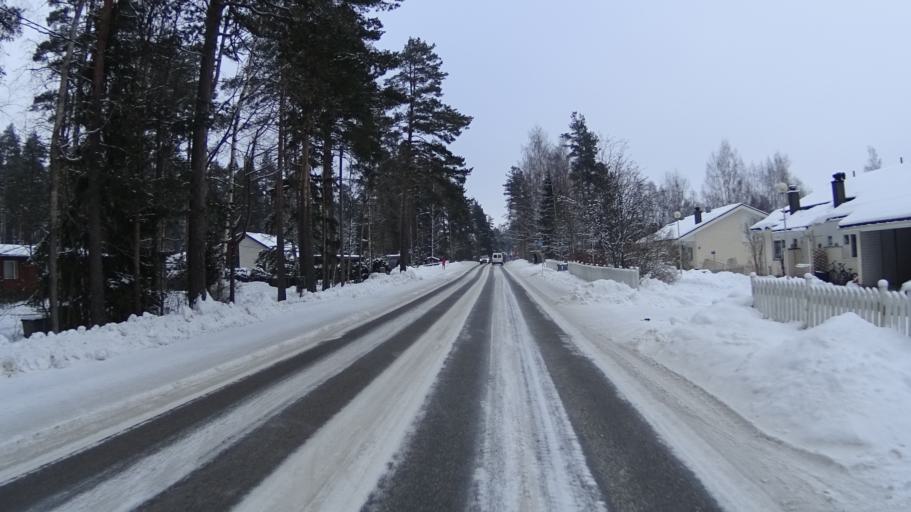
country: FI
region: Uusimaa
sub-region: Helsinki
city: Vihti
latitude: 60.3326
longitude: 24.3046
